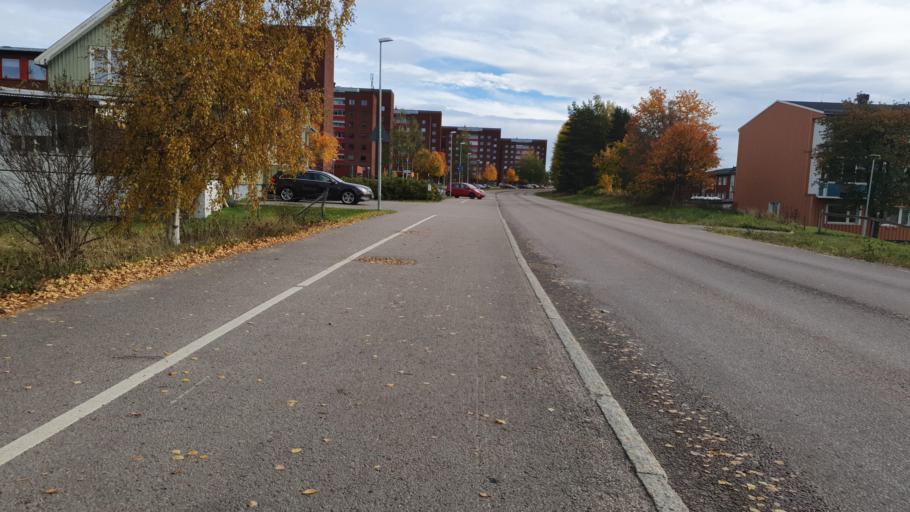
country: SE
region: Vaesternorrland
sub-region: Sundsvalls Kommun
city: Sundsvall
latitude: 62.4050
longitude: 17.2462
